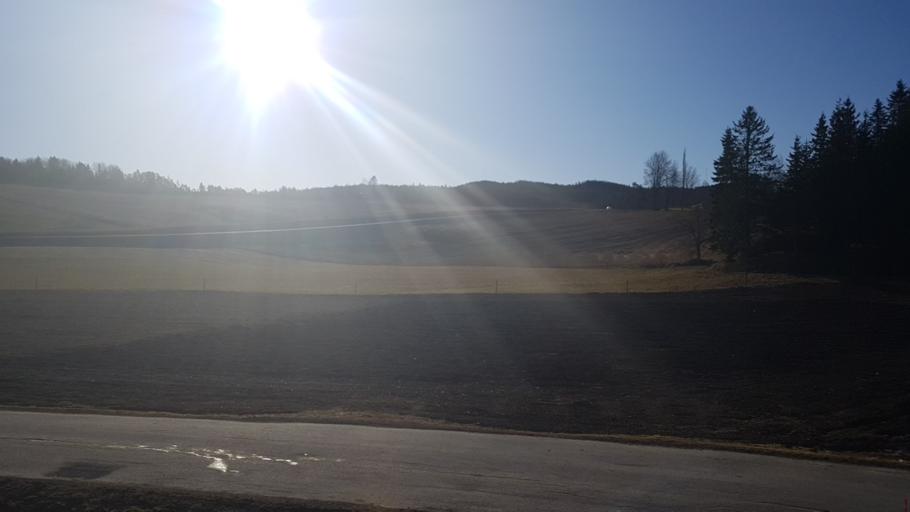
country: NO
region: Nord-Trondelag
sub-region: Levanger
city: Skogn
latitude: 63.6730
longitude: 11.1138
